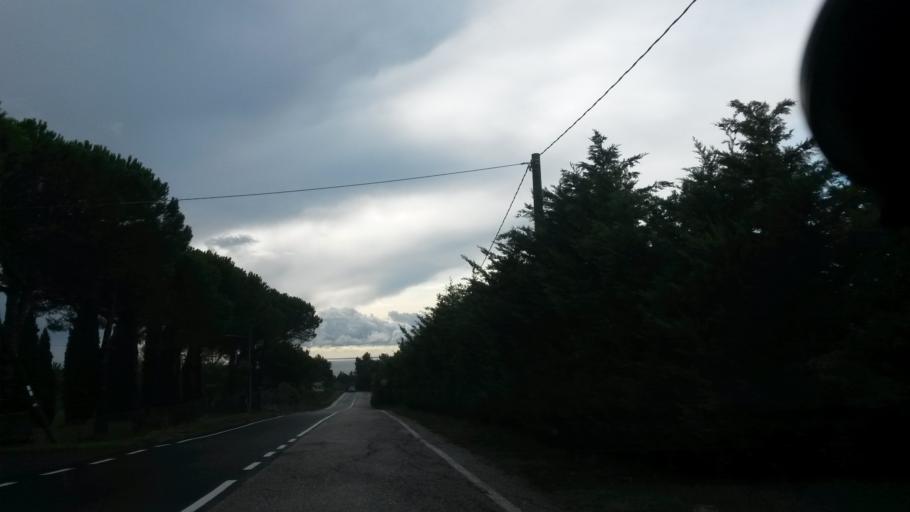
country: IT
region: Tuscany
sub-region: Provincia di Livorno
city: Rosignano Marittimo
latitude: 43.4170
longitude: 10.4538
